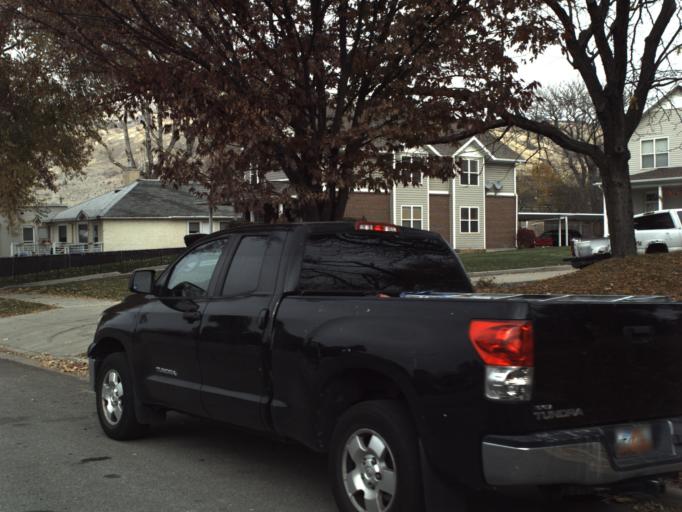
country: US
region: Utah
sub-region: Salt Lake County
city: Salt Lake City
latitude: 40.7788
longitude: -111.9024
